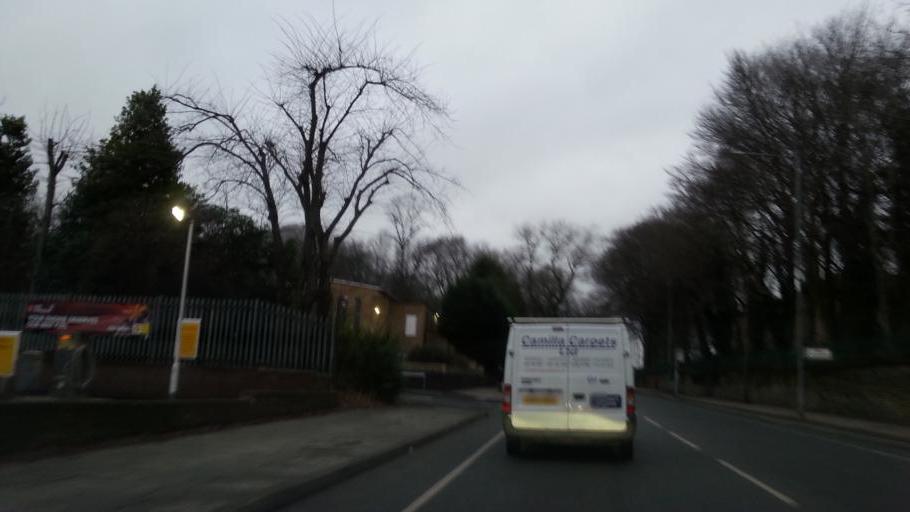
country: GB
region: England
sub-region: Borough of Bury
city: Prestwich
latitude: 53.5208
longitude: -2.2732
